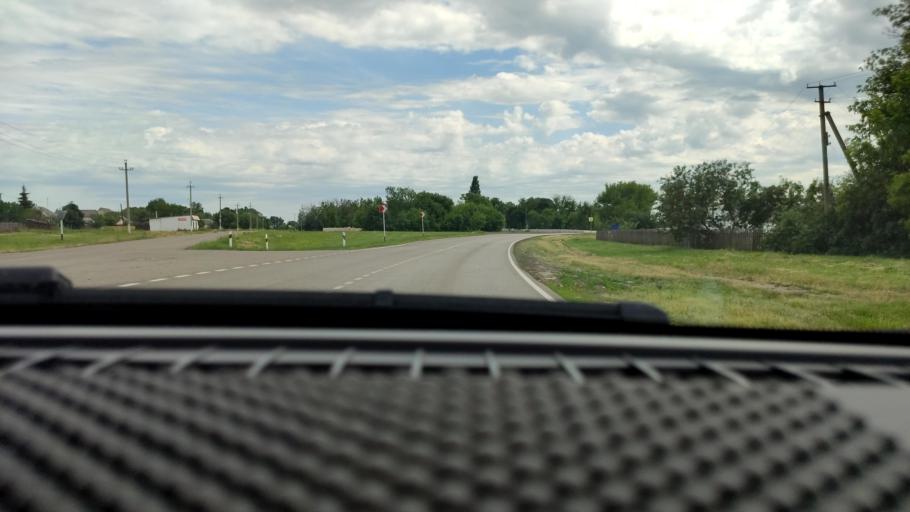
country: RU
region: Voronezj
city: Verkhnyaya Khava
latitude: 51.6805
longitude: 39.9411
